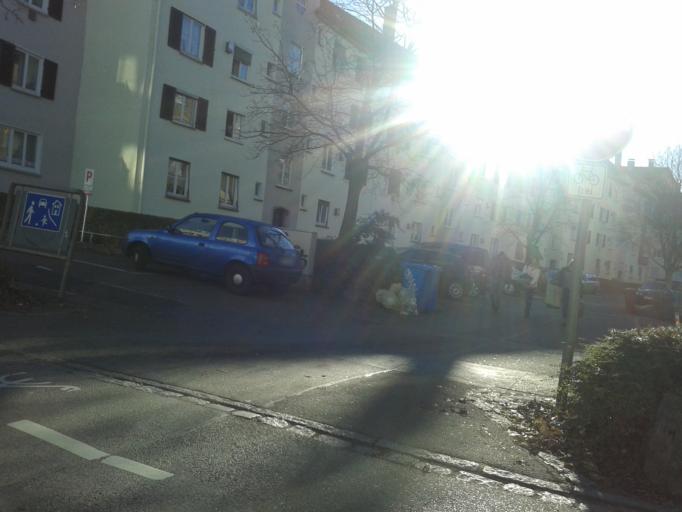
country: DE
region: Baden-Wuerttemberg
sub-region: Tuebingen Region
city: Ulm
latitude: 48.3954
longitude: 9.9714
